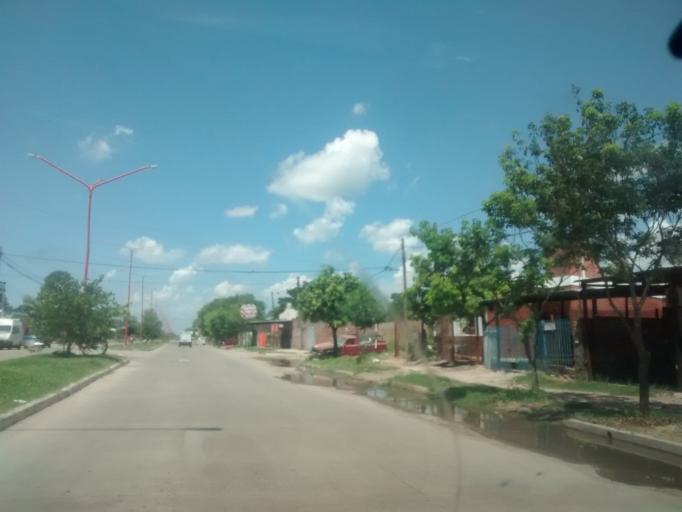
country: AR
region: Chaco
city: Resistencia
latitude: -27.4739
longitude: -58.9925
